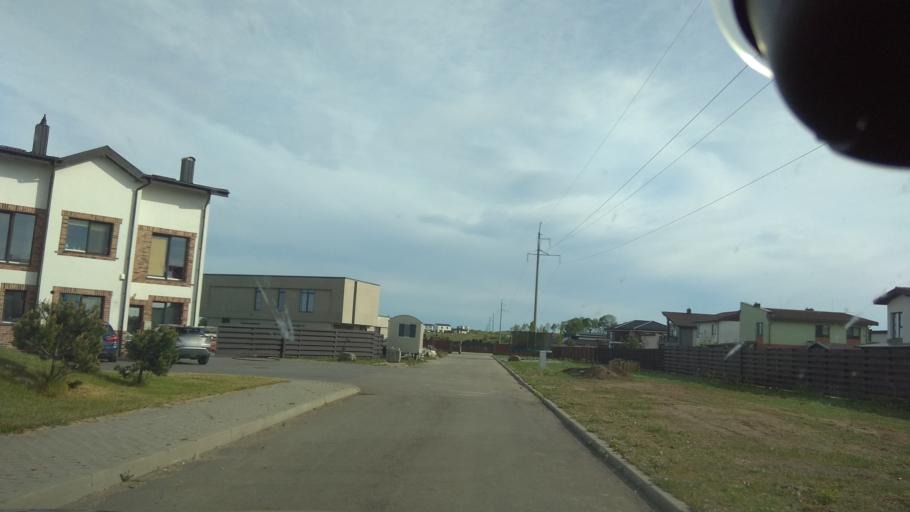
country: LT
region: Klaipedos apskritis
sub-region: Klaipeda
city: Klaipeda
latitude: 55.7487
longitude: 21.1826
